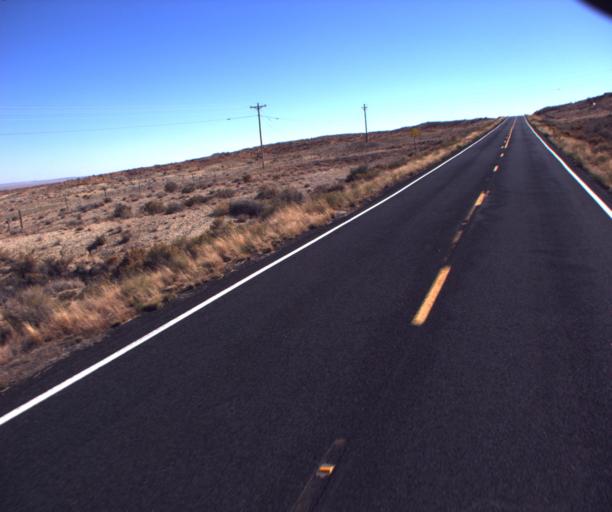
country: US
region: Arizona
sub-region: Coconino County
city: Tuba City
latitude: 35.9954
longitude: -111.0241
